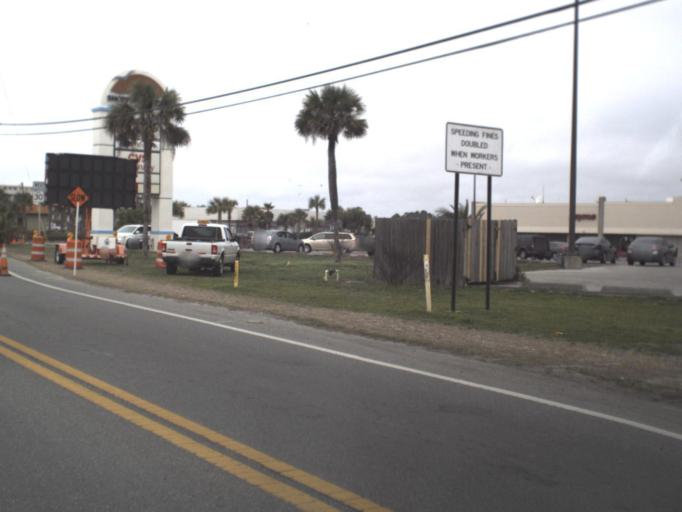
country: US
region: Florida
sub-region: Bay County
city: Laguna Beach
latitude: 30.2236
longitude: -85.8919
